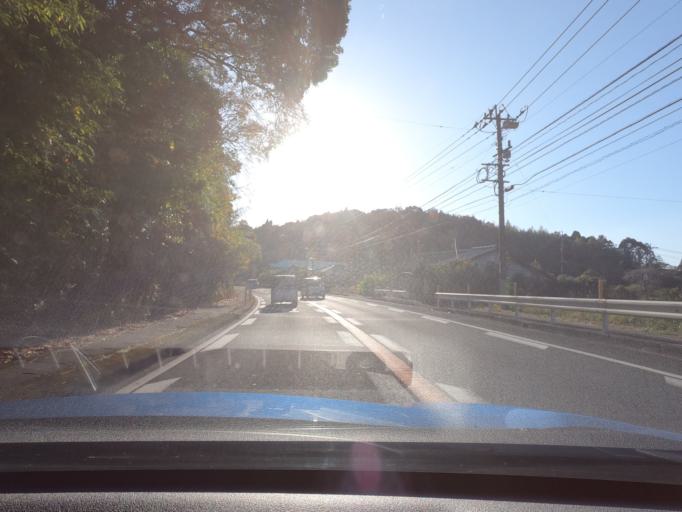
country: JP
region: Kagoshima
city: Akune
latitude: 32.0460
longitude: 130.2168
